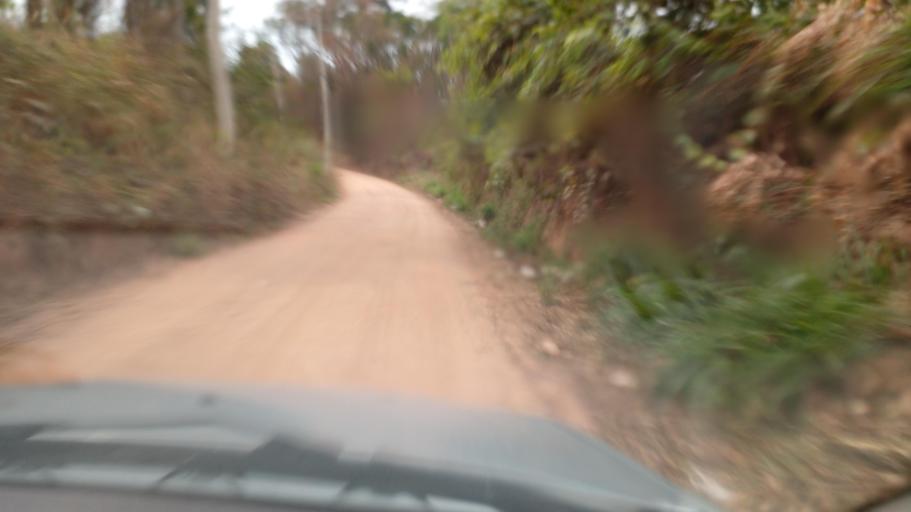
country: BR
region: Sao Paulo
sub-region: Louveira
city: Louveira
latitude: -23.1298
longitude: -46.9079
